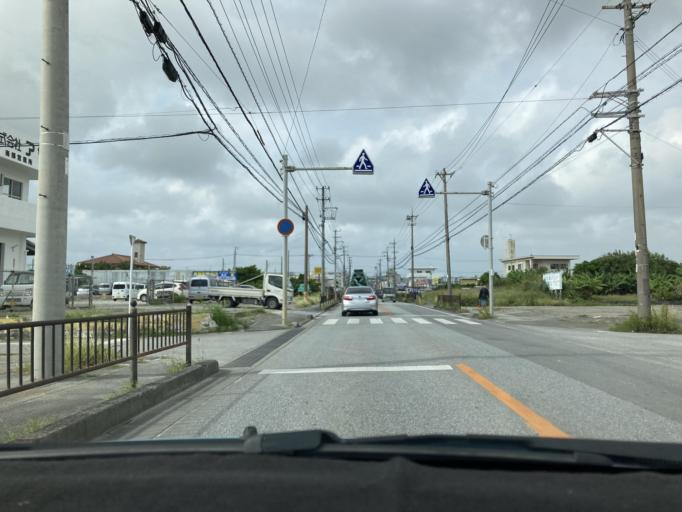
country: JP
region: Okinawa
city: Tomigusuku
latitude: 26.1659
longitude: 127.6683
